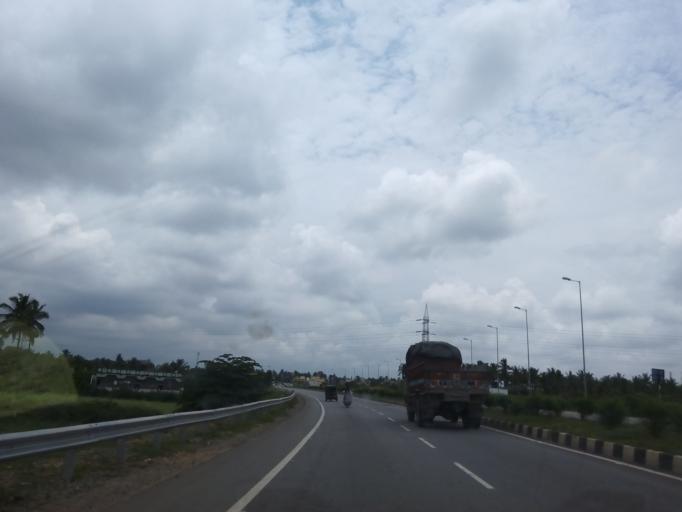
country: IN
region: Karnataka
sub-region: Hassan
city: Hassan
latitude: 12.9994
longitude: 76.1459
